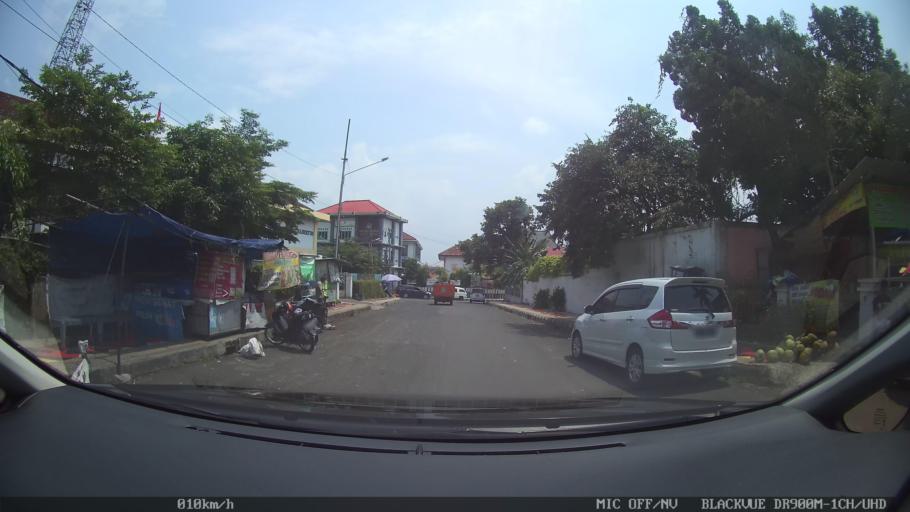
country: ID
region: Lampung
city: Bandarlampung
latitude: -5.4259
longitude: 105.2687
